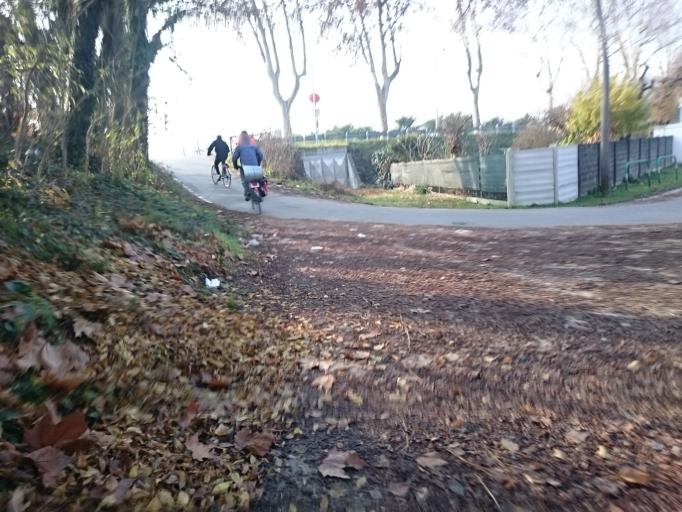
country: IT
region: Veneto
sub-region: Provincia di Padova
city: Noventa
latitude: 45.4050
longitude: 11.9216
